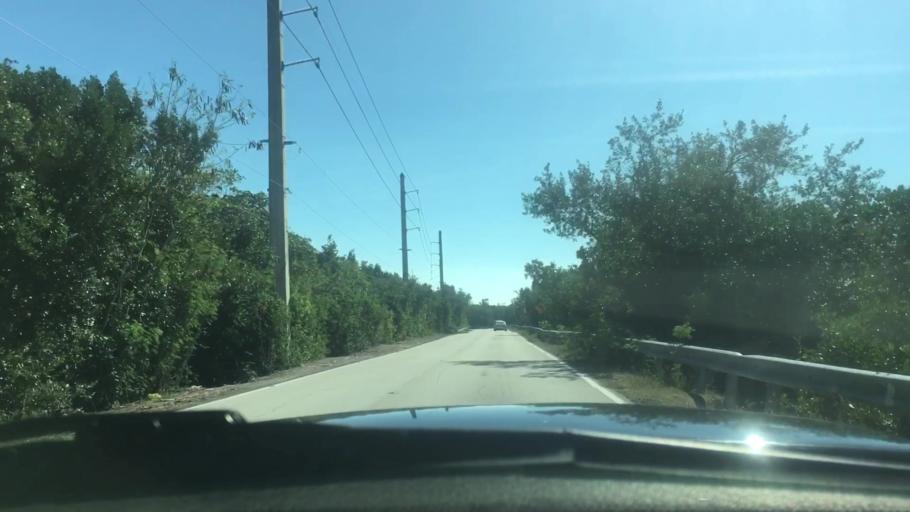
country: US
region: Florida
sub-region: Monroe County
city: North Key Largo
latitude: 25.2940
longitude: -80.3827
